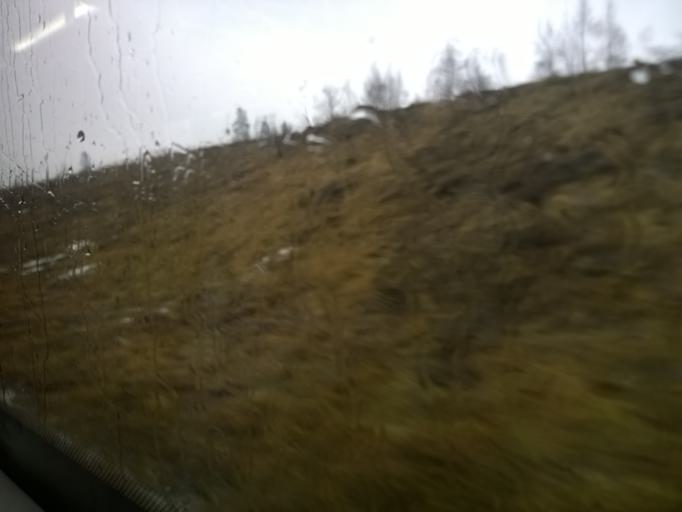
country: FI
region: Pirkanmaa
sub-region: Tampere
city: Tampere
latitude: 61.4307
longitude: 23.8230
